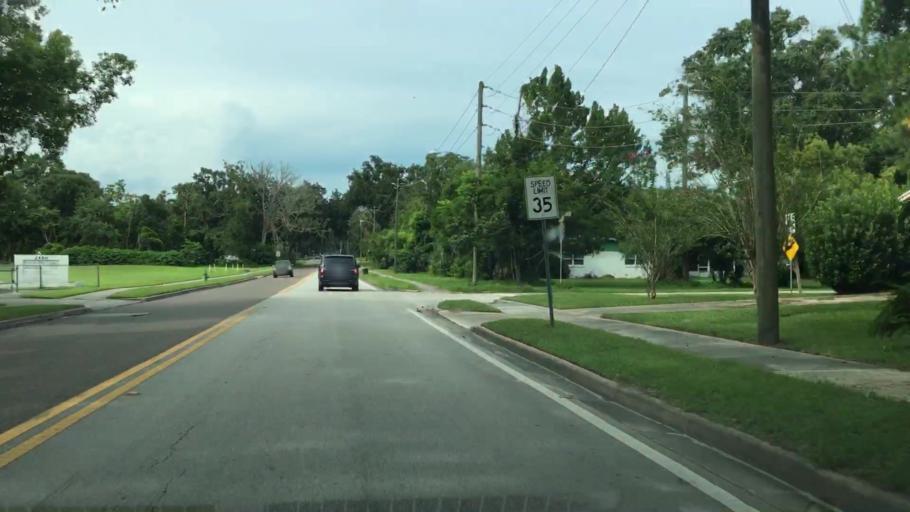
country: US
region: Florida
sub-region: Seminole County
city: Sanford
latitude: 28.7880
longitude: -81.2648
